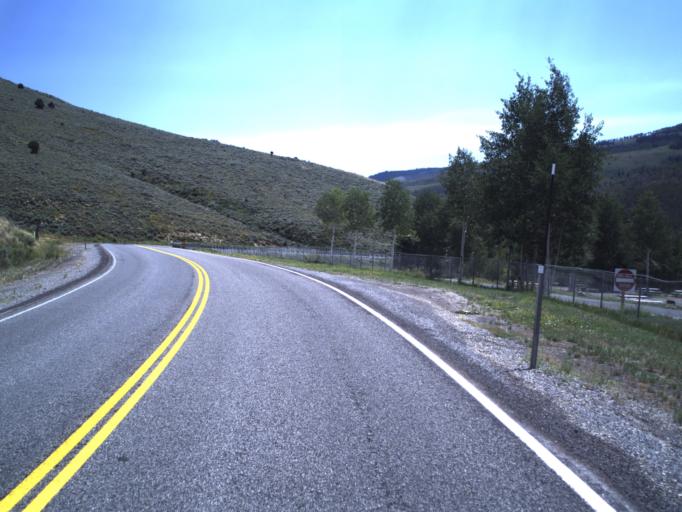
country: US
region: Utah
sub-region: Carbon County
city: Helper
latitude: 39.7911
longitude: -111.1311
